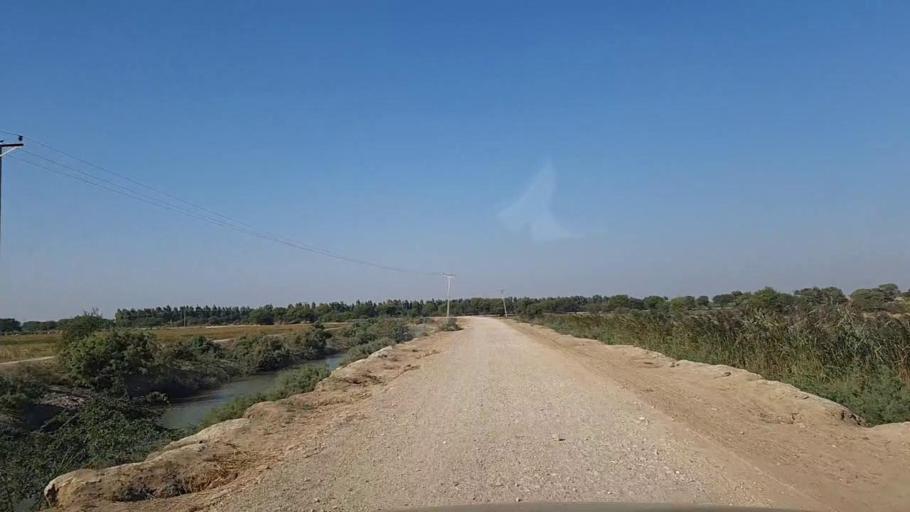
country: PK
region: Sindh
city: Mirpur Batoro
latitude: 24.7331
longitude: 68.3454
